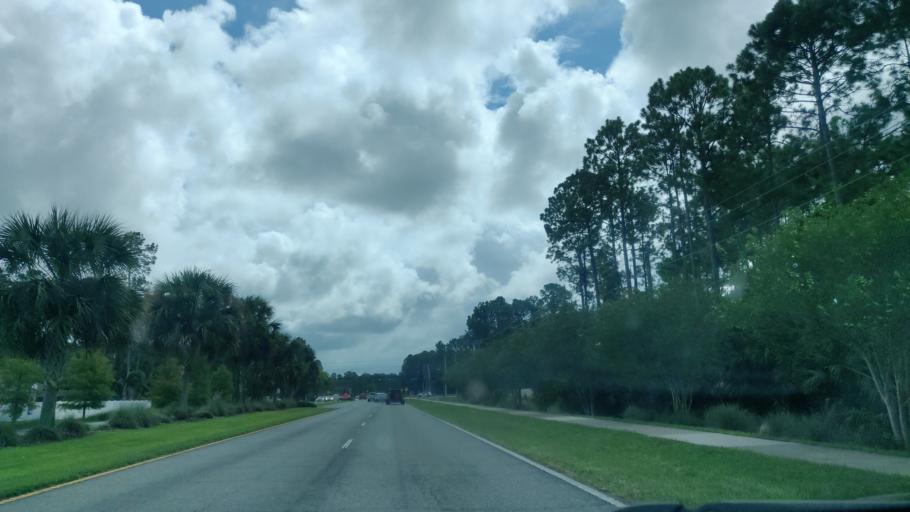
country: US
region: Florida
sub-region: Flagler County
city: Bunnell
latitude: 29.4996
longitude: -81.2199
